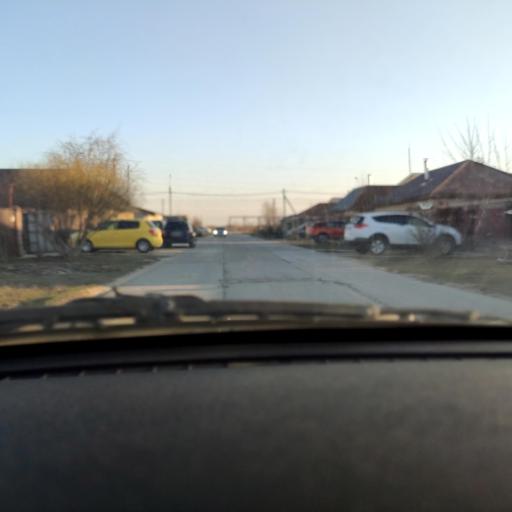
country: RU
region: Samara
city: Podstepki
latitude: 53.5706
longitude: 49.1189
